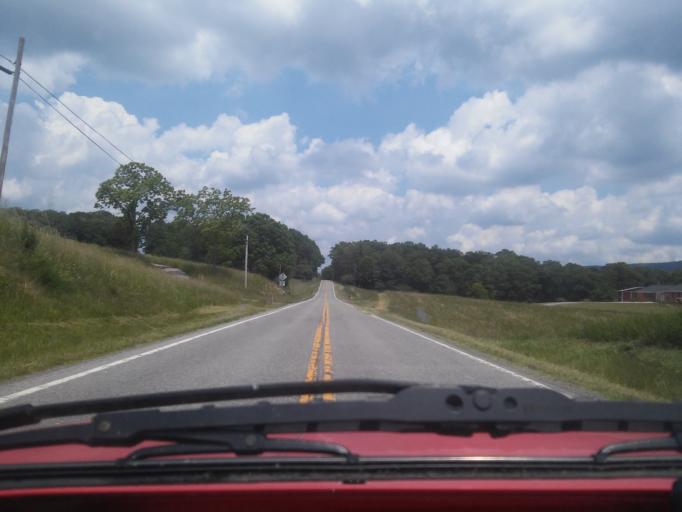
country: US
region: Virginia
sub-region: Craig County
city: New Castle
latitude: 37.4617
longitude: -80.1739
